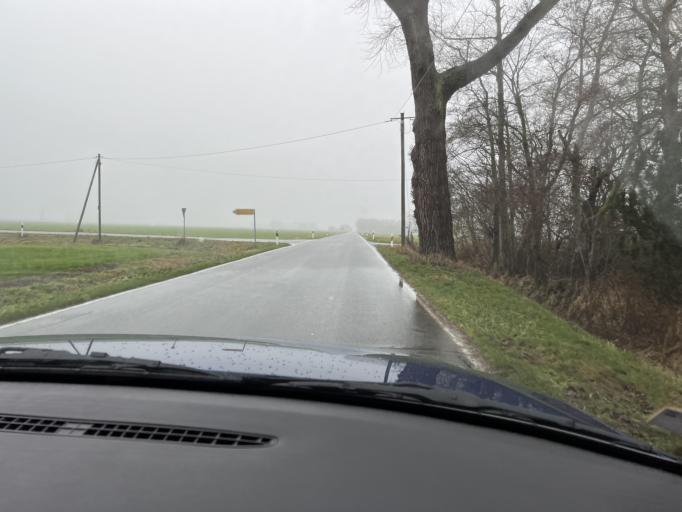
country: DE
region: Schleswig-Holstein
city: Schulp
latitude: 54.2565
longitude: 8.9111
